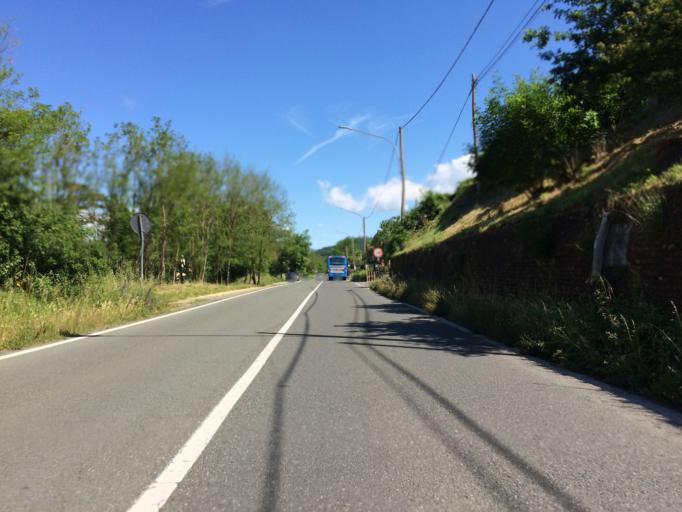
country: IT
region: Tuscany
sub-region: Provincia di Massa-Carrara
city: Terrarossa
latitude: 44.2362
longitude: 9.9601
